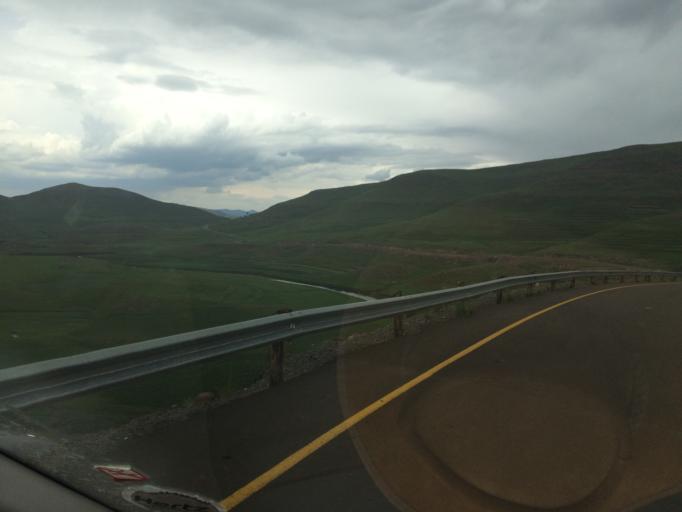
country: LS
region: Maseru
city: Nako
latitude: -29.7836
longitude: 28.0236
